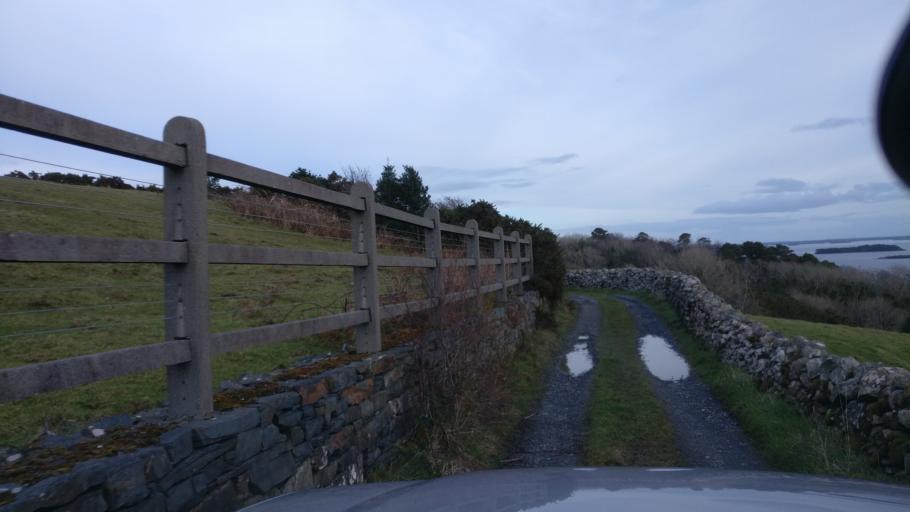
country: IE
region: Connaught
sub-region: County Galway
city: Oughterard
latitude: 53.5246
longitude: -9.3814
